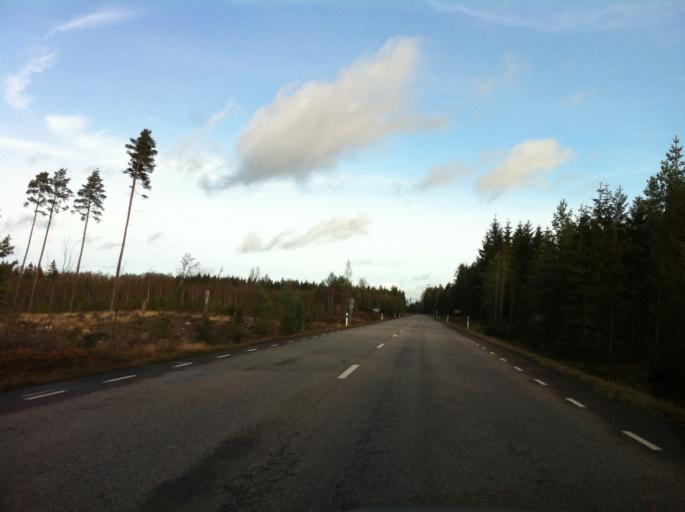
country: SE
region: Kronoberg
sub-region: Almhults Kommun
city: AElmhult
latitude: 56.5973
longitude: 14.2126
